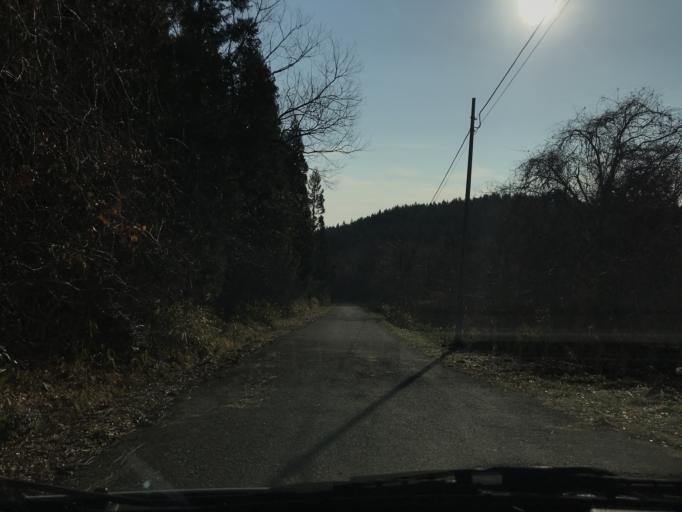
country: JP
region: Iwate
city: Ichinoseki
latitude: 38.9740
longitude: 141.0459
